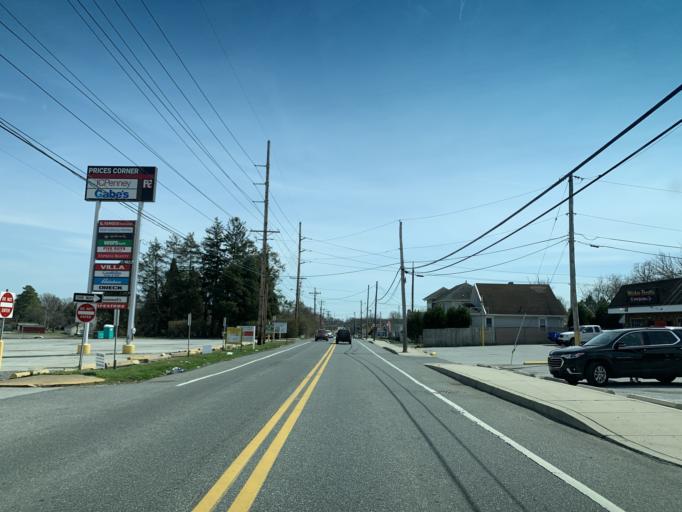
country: US
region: Delaware
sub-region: New Castle County
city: Newport
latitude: 39.7341
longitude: -75.6286
